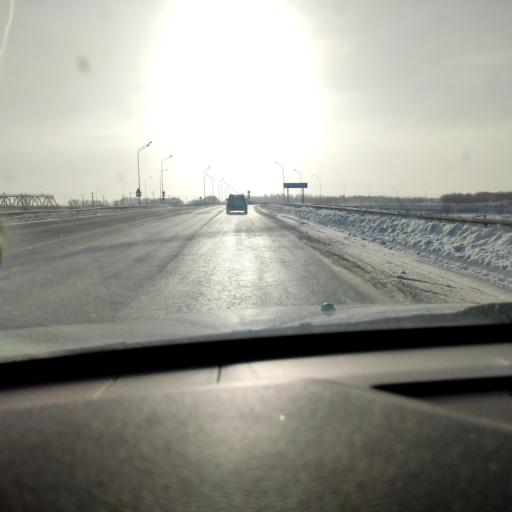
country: RU
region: Samara
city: Smyshlyayevka
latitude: 53.1520
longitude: 50.3836
